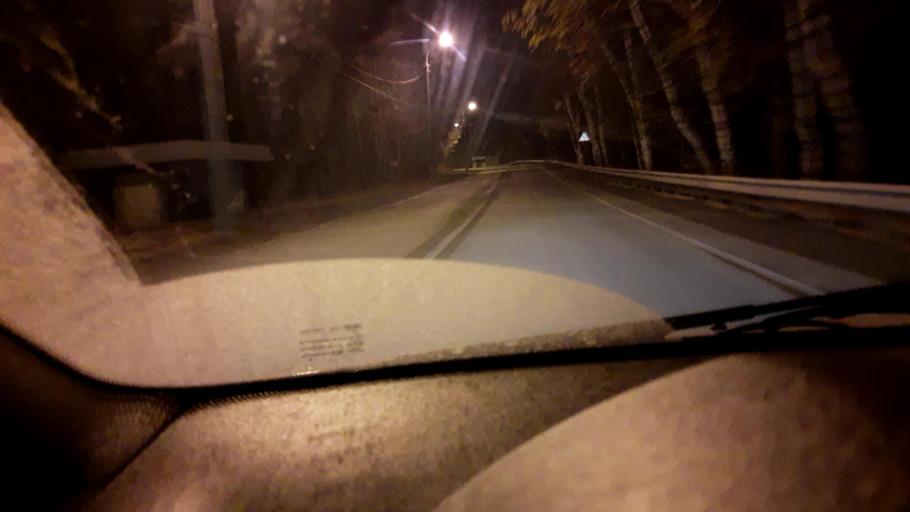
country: RU
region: Bashkortostan
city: Ufa
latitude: 54.8549
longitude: 56.0734
